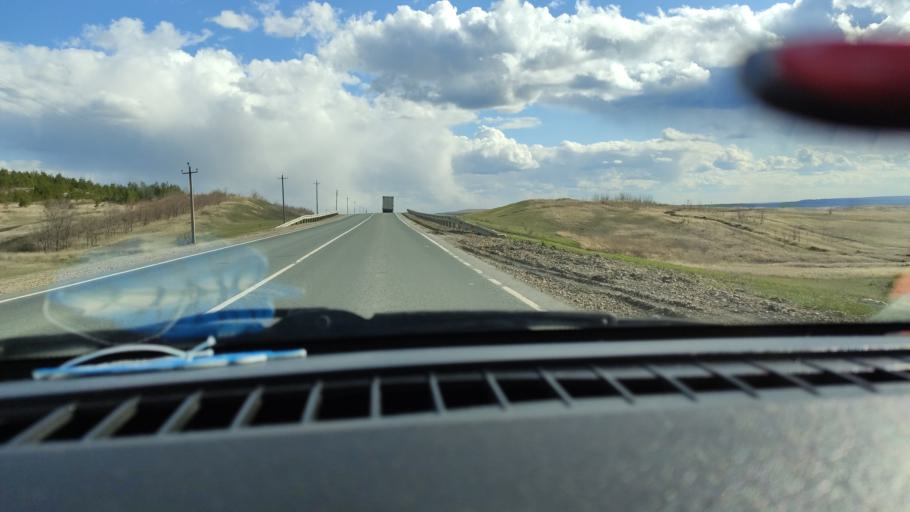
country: RU
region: Saratov
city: Alekseyevka
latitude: 52.2982
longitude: 47.9278
